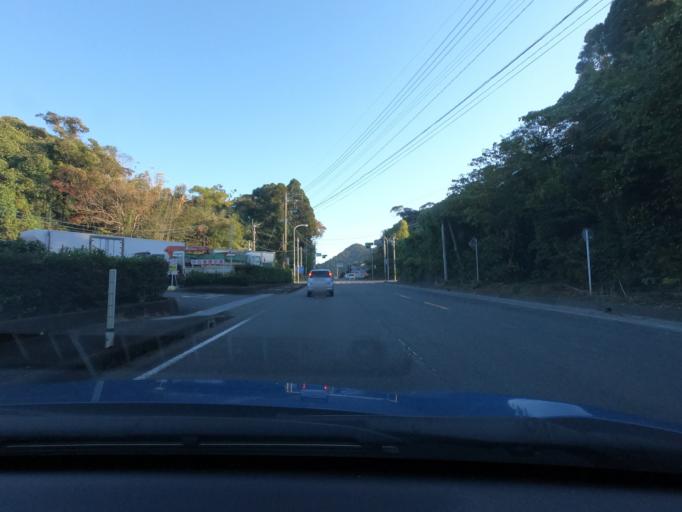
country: JP
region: Kagoshima
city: Satsumasendai
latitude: 31.8587
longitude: 130.2313
